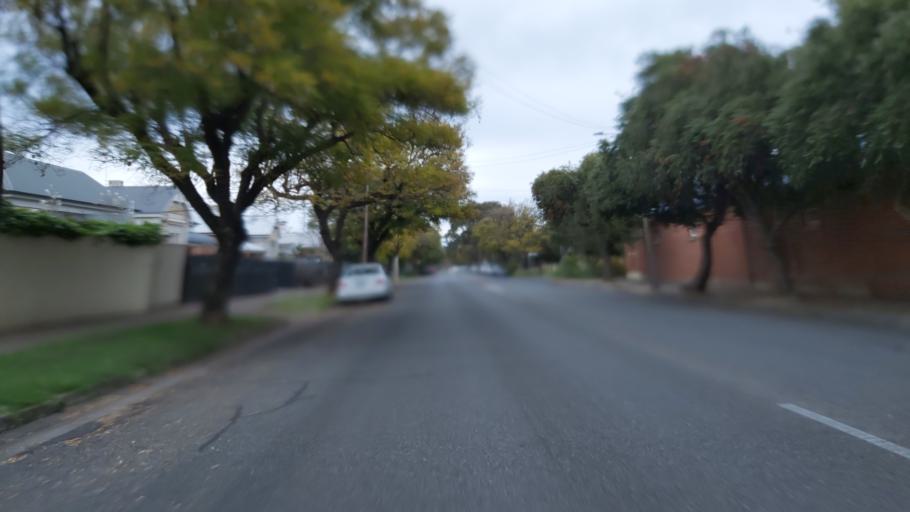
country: AU
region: South Australia
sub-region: Unley
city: Unley
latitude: -34.9515
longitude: 138.6117
